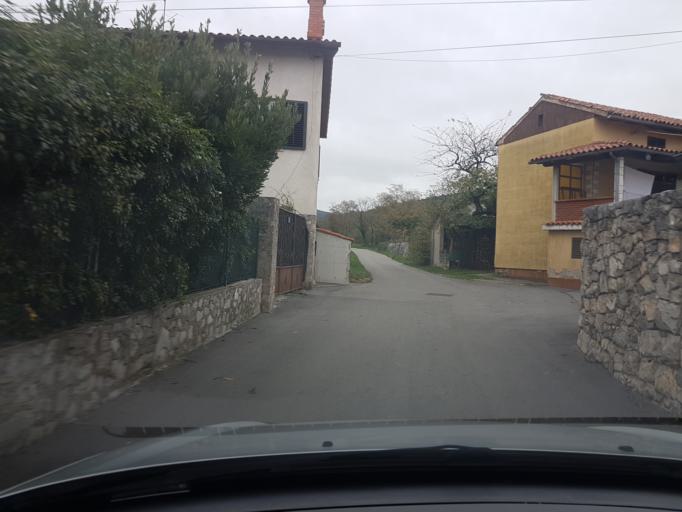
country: SI
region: Sezana
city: Sezana
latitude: 45.7373
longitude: 13.9302
